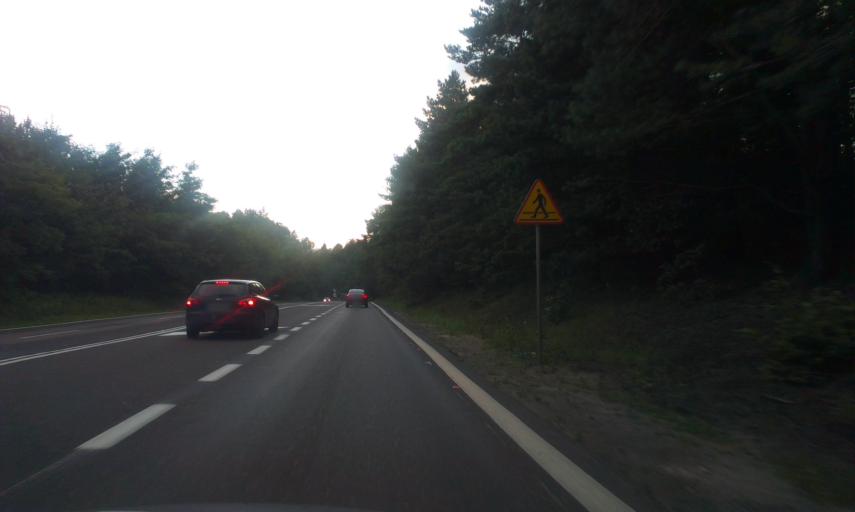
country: PL
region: West Pomeranian Voivodeship
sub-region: Koszalin
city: Koszalin
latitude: 54.2213
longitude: 16.2284
